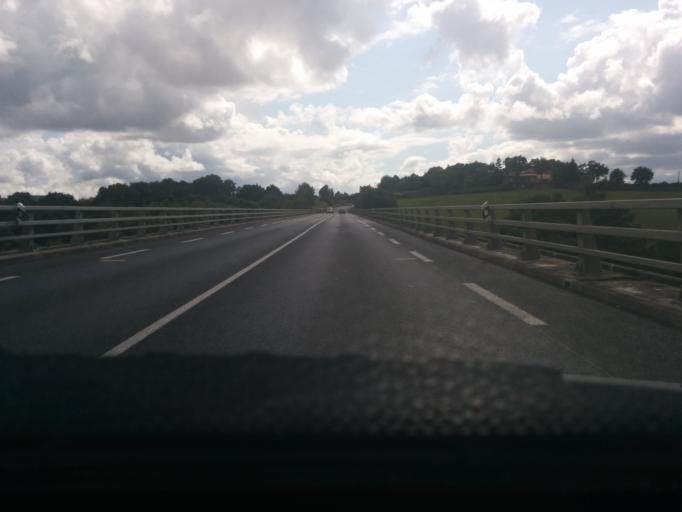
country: FR
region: Pays de la Loire
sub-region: Departement de la Vendee
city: Mortagne-sur-Sevre
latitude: 46.9821
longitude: -0.9522
